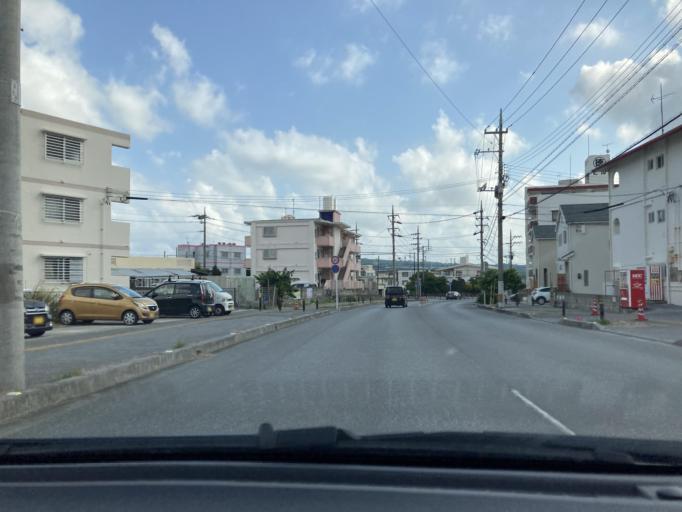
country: JP
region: Okinawa
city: Tomigusuku
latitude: 26.1528
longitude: 127.7176
